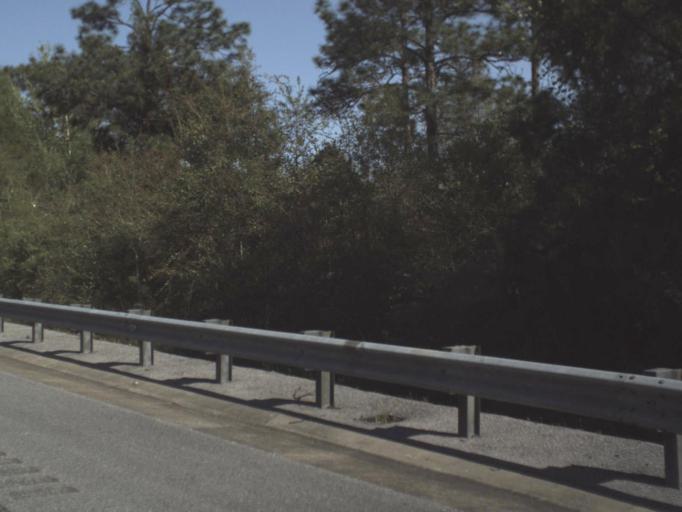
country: US
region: Florida
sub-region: Okaloosa County
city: Crestview
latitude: 30.7254
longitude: -86.5756
